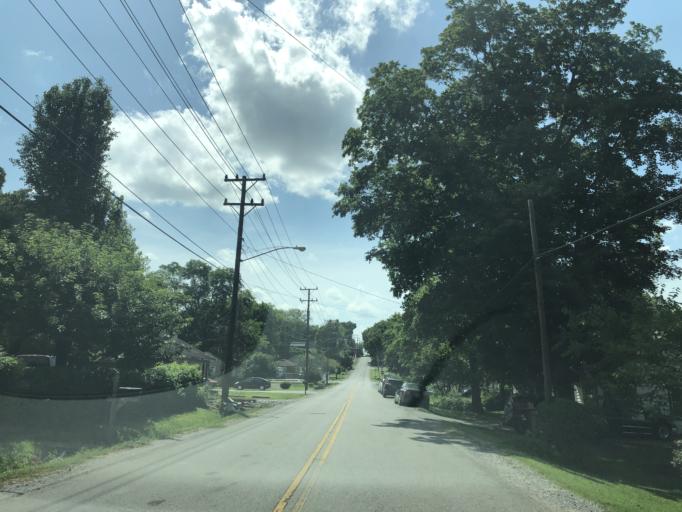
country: US
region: Tennessee
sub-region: Davidson County
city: Oak Hill
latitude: 36.0977
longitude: -86.7409
